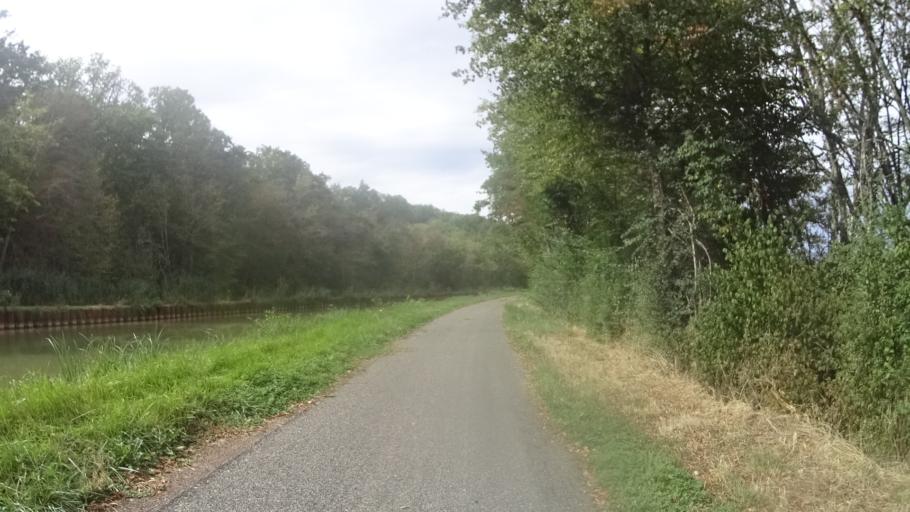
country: FR
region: Bourgogne
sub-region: Departement de la Nievre
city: Sermoise-sur-Loire
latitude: 46.9391
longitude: 3.2025
